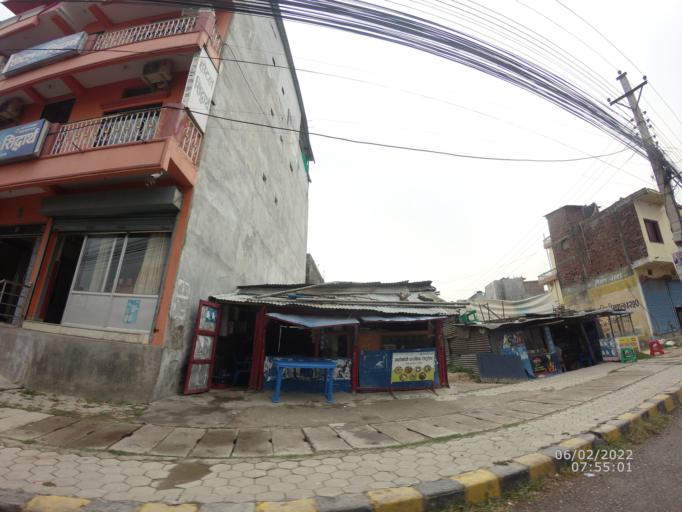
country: NP
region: Western Region
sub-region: Lumbini Zone
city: Bhairahawa
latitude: 27.4977
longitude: 83.4590
